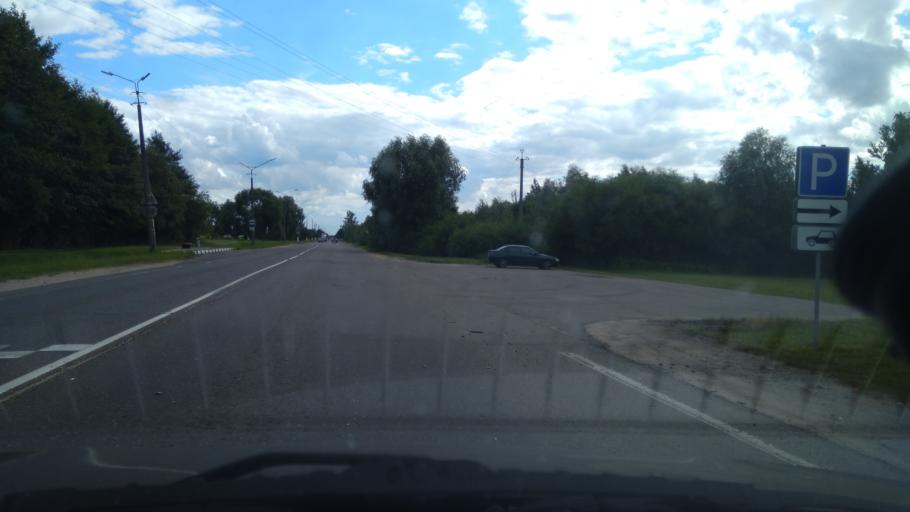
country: BY
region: Grodnenskaya
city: Masty
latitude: 53.4229
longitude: 24.5392
